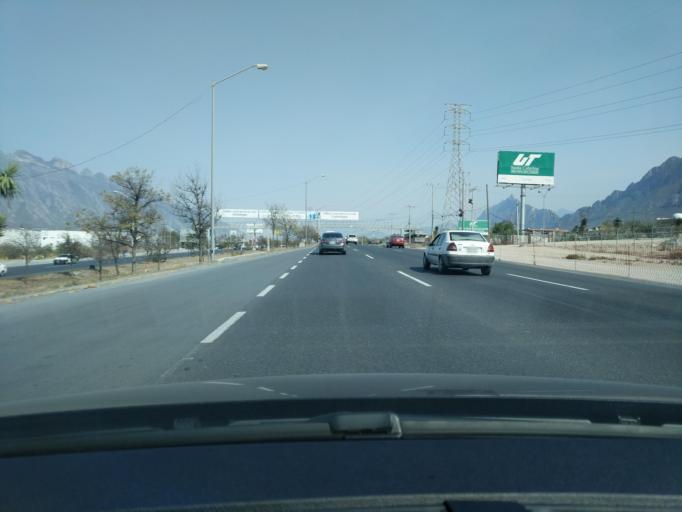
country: MX
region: Nuevo Leon
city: Santa Catarina
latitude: 25.6931
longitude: -100.5129
